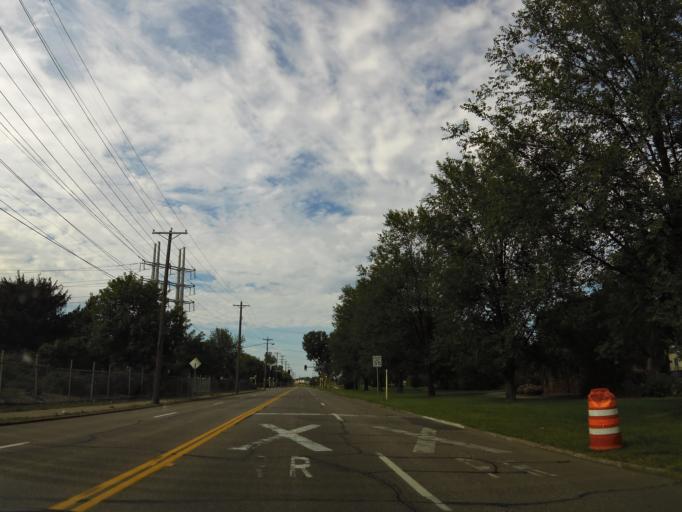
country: US
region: Minnesota
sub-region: Anoka County
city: Columbia Heights
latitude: 45.0226
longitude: -93.2732
